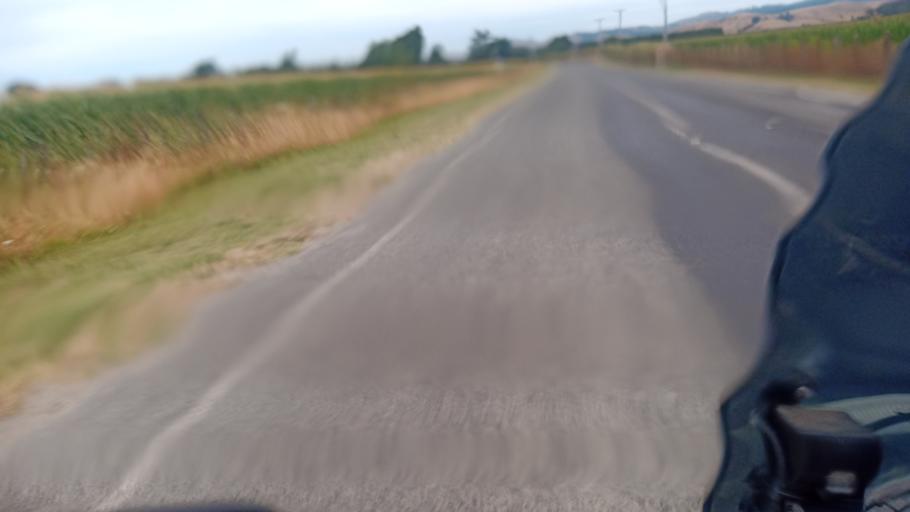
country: NZ
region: Gisborne
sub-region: Gisborne District
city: Gisborne
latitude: -38.6055
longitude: 177.8959
